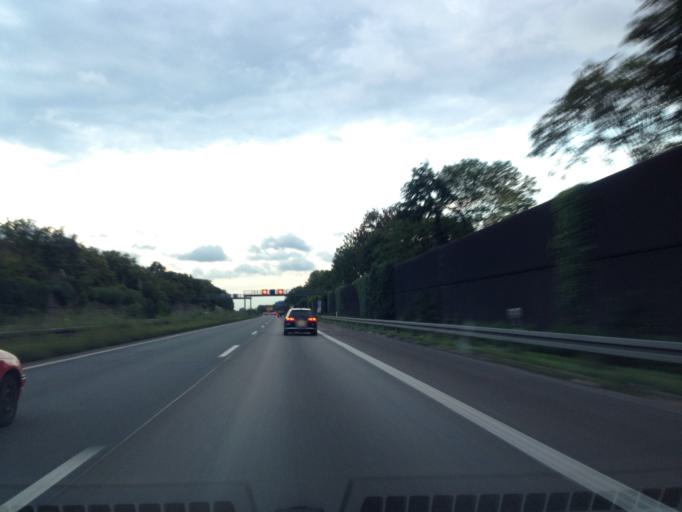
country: DE
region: North Rhine-Westphalia
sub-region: Regierungsbezirk Dusseldorf
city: Krefeld
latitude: 51.3606
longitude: 6.6268
